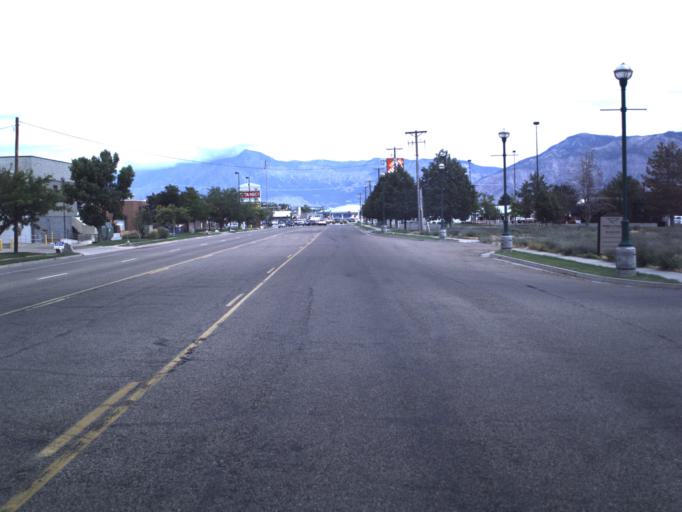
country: US
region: Utah
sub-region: Weber County
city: Riverdale
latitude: 41.1739
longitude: -112.0047
